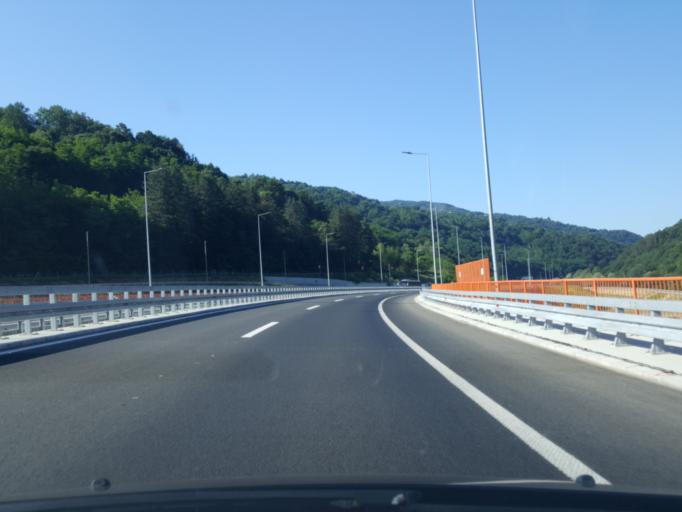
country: RS
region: Central Serbia
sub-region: Pcinjski Okrug
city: Vladicin Han
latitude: 42.8183
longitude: 22.1210
